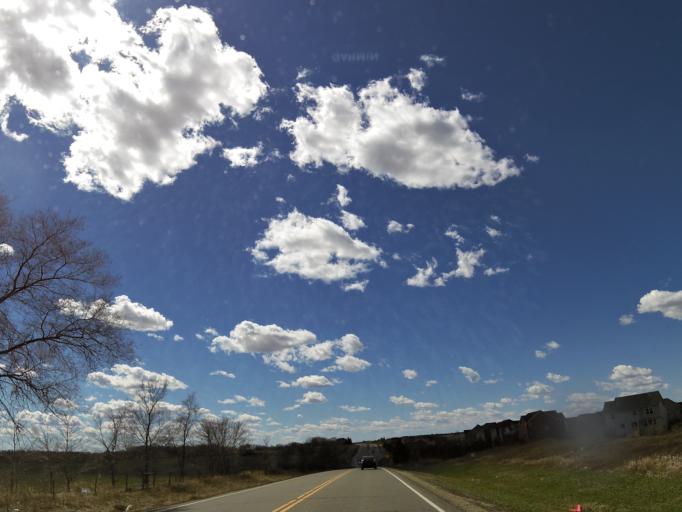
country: US
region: Minnesota
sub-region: Dakota County
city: Apple Valley
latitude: 44.6931
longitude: -93.2259
